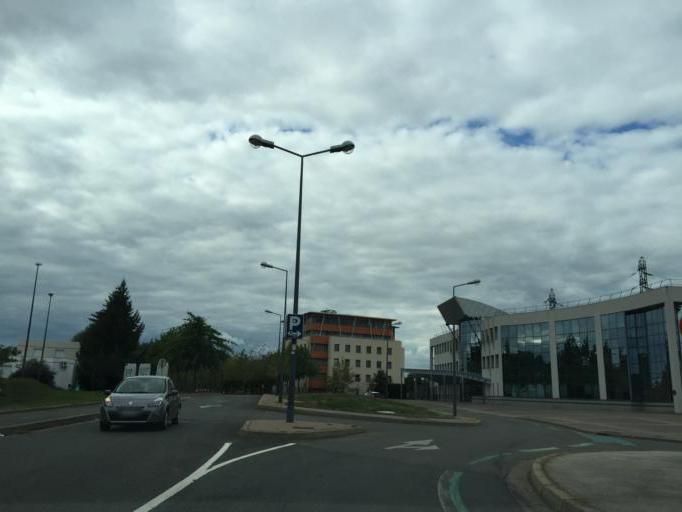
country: FR
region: Rhone-Alpes
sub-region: Departement de la Loire
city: Saint-Etienne
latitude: 45.4576
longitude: 4.3972
